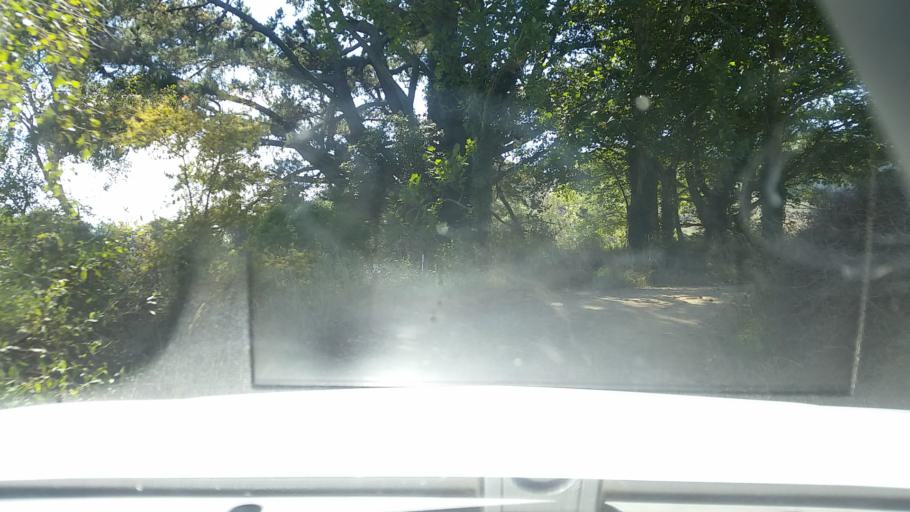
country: NZ
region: Nelson
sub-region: Nelson City
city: Nelson
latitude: -41.2487
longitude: 173.5849
